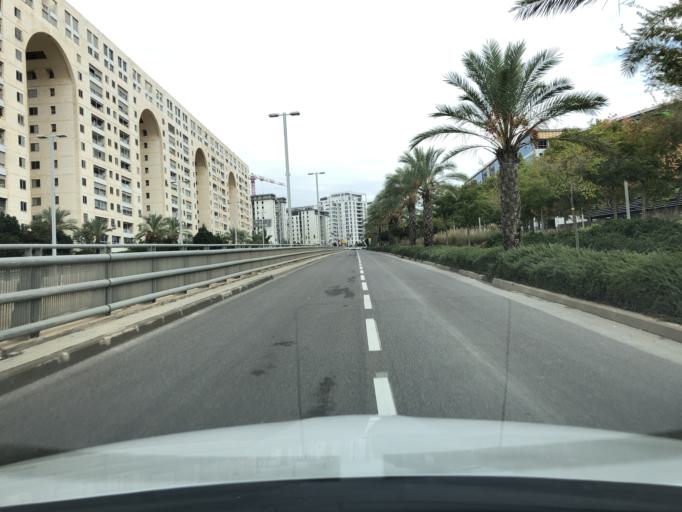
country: IL
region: Central District
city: Modiin
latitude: 31.9036
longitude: 35.0052
